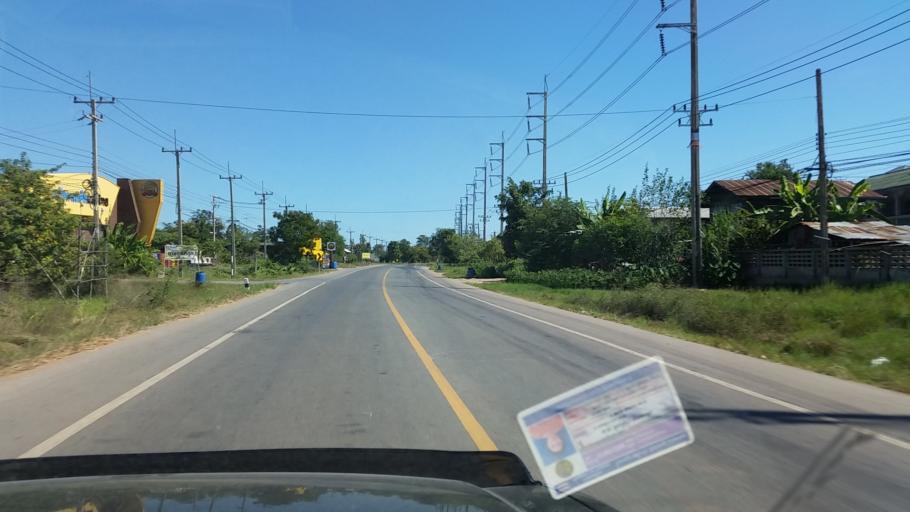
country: TH
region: Chaiyaphum
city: Ban Khwao
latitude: 15.7858
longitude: 101.9586
